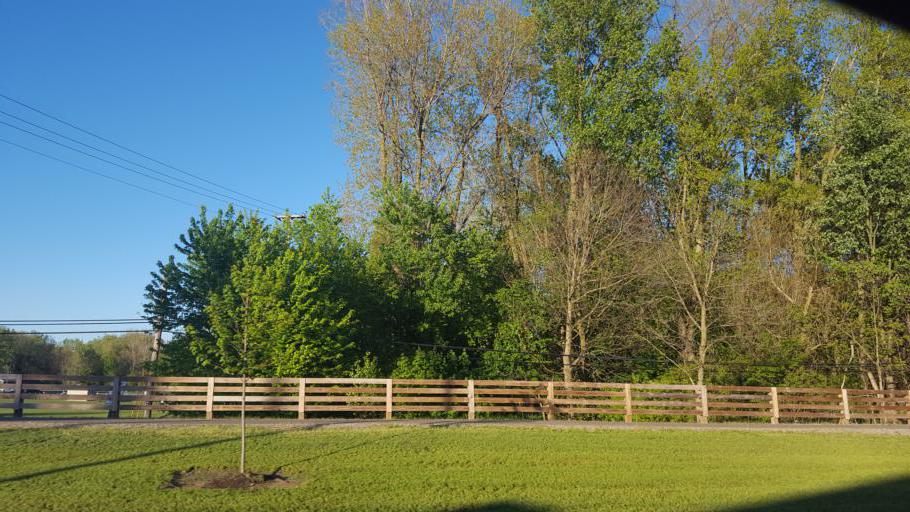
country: US
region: Ohio
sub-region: Knox County
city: Fredericktown
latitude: 40.4857
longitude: -82.5445
